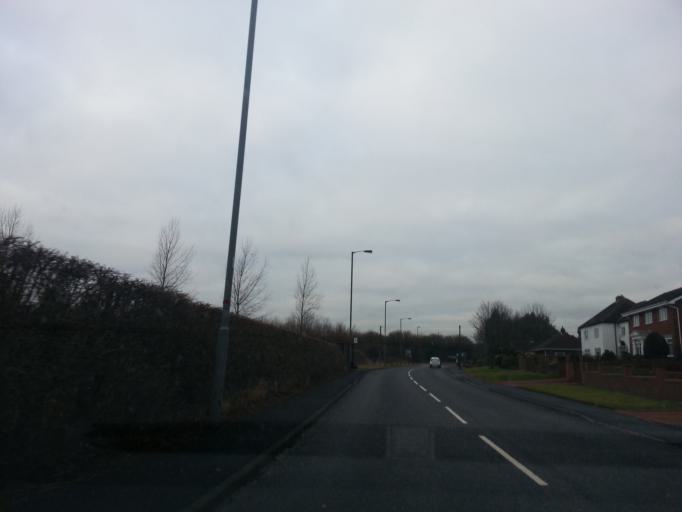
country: GB
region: England
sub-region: County Durham
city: Chester-le-Street
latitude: 54.8761
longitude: -1.5620
